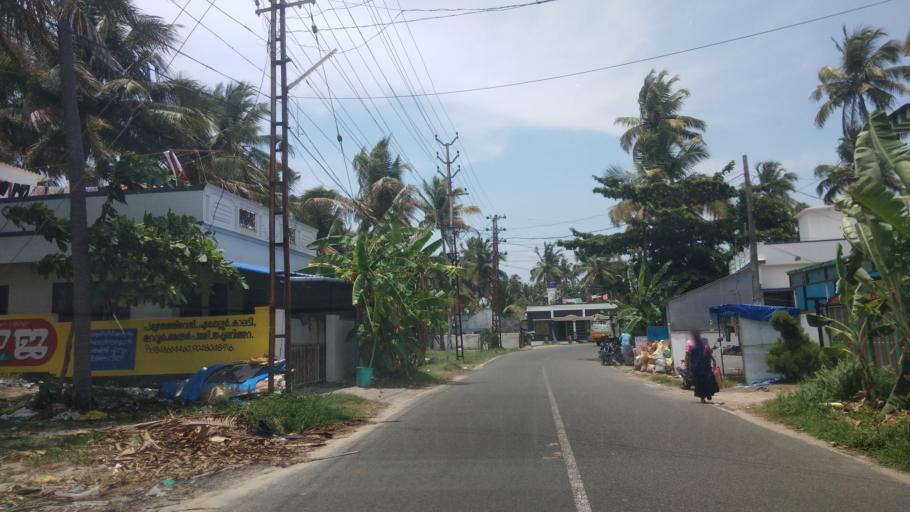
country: IN
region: Kerala
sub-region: Alappuzha
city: Arukutti
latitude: 9.8545
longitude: 76.2654
